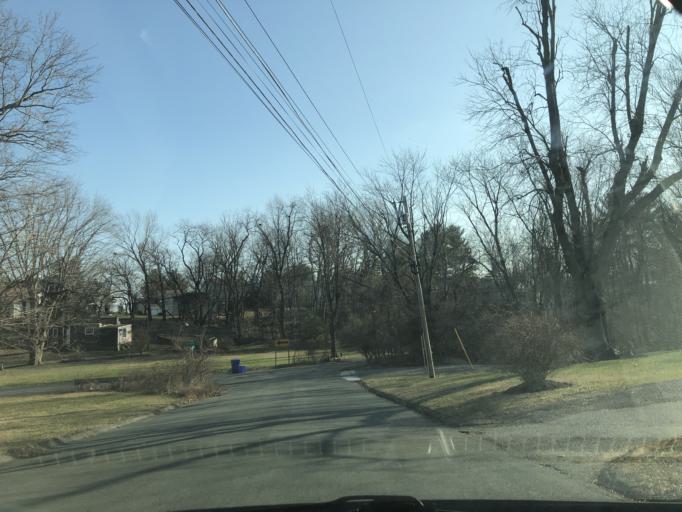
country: US
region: Maryland
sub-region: Montgomery County
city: Burtonsville
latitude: 39.1050
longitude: -76.9357
